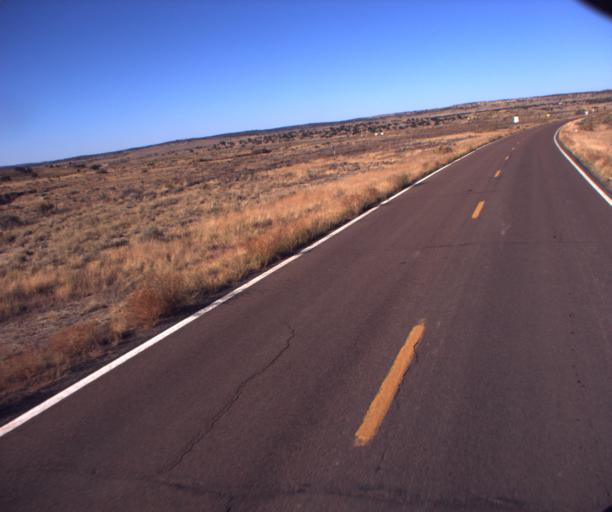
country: US
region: Arizona
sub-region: Apache County
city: Ganado
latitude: 35.7465
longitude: -109.8659
